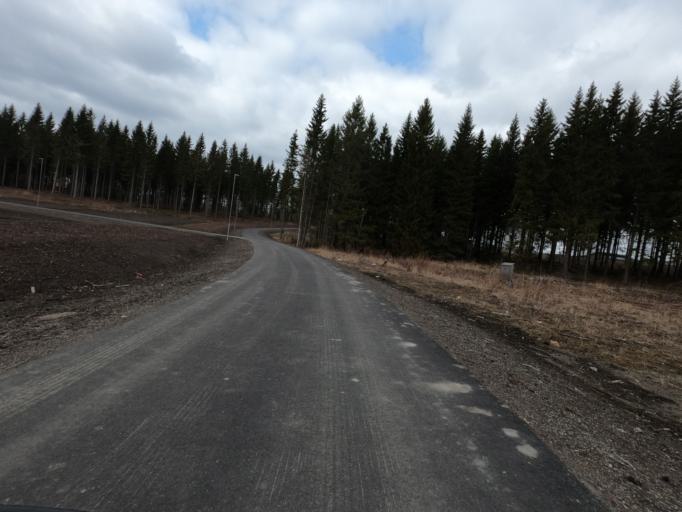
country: FI
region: North Karelia
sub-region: Joensuu
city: Joensuu
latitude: 62.5601
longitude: 29.8234
